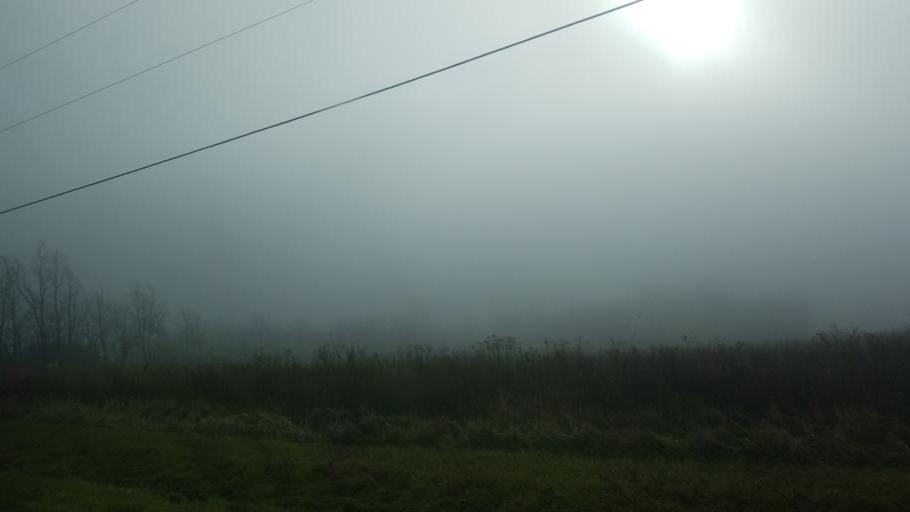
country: US
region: Ohio
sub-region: Champaign County
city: North Lewisburg
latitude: 40.3069
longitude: -83.6142
